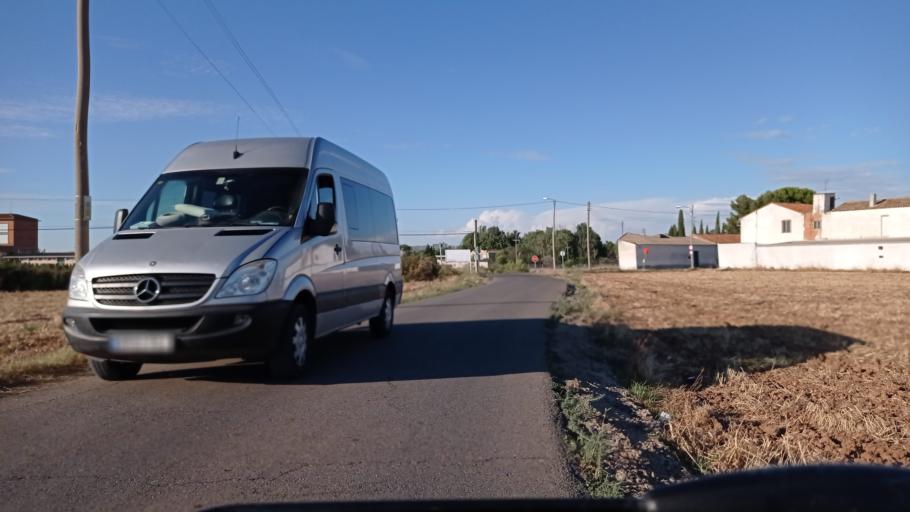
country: ES
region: Aragon
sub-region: Provincia de Zaragoza
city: Oliver-Valdefierro, Oliver, Valdefierro
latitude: 41.6756
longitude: -0.9658
